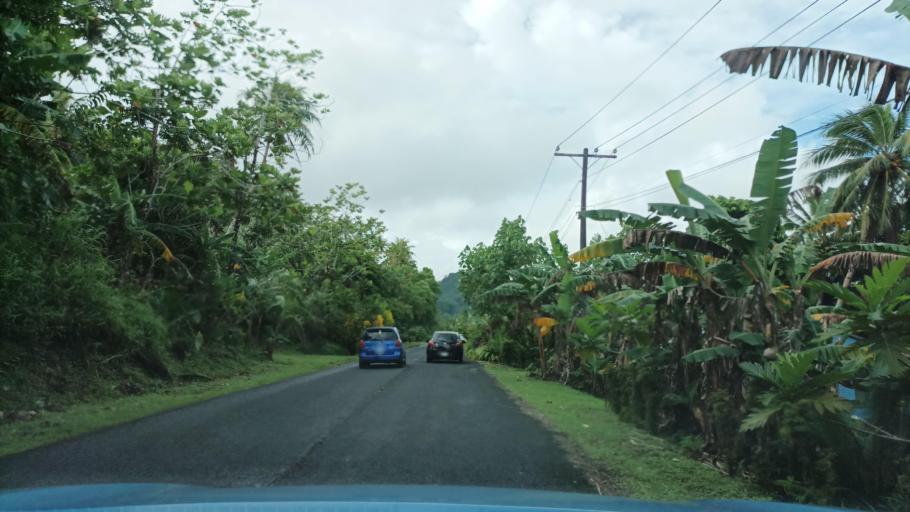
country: FM
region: Pohnpei
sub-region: Kolonia Municipality
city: Kolonia
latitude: 6.9660
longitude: 158.2513
